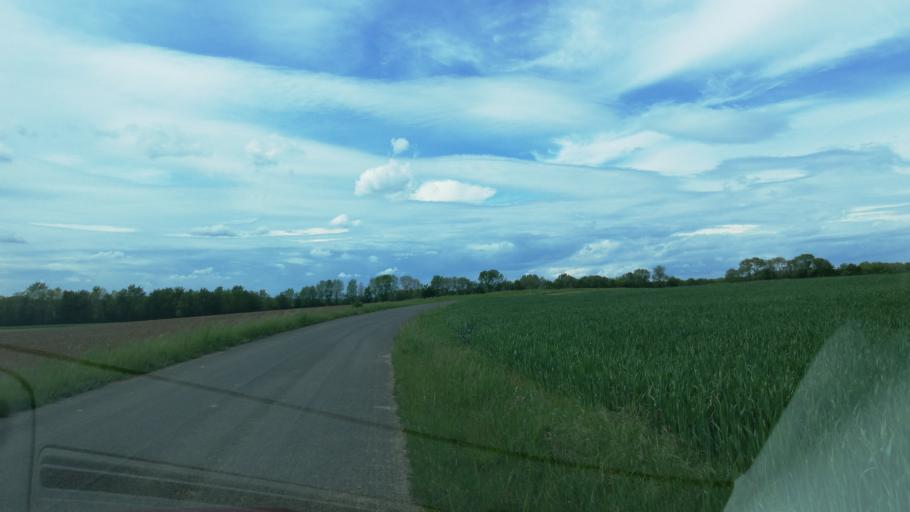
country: AT
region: Burgenland
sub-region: Politischer Bezirk Oberpullendorf
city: Lutzmannsburg
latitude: 47.4553
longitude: 16.6054
